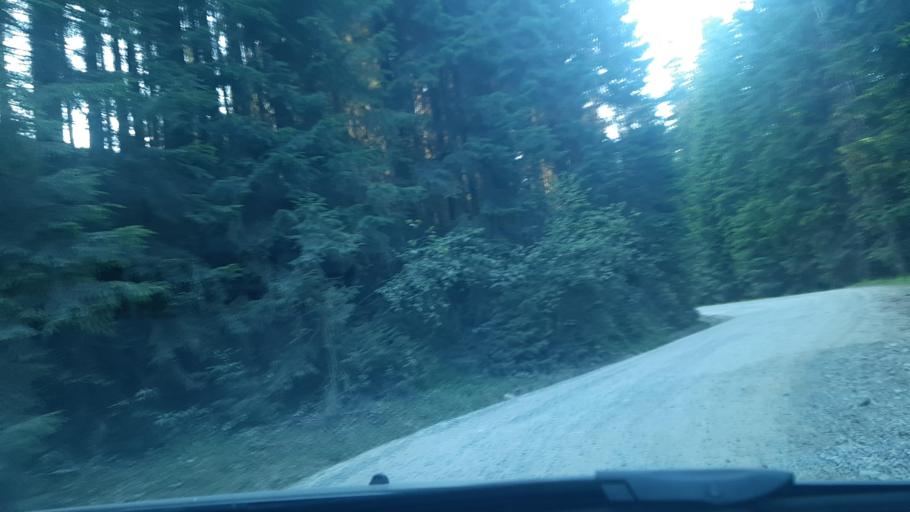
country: RO
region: Alba
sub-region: Comuna Sugag
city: Sugag
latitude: 45.5782
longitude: 23.6080
